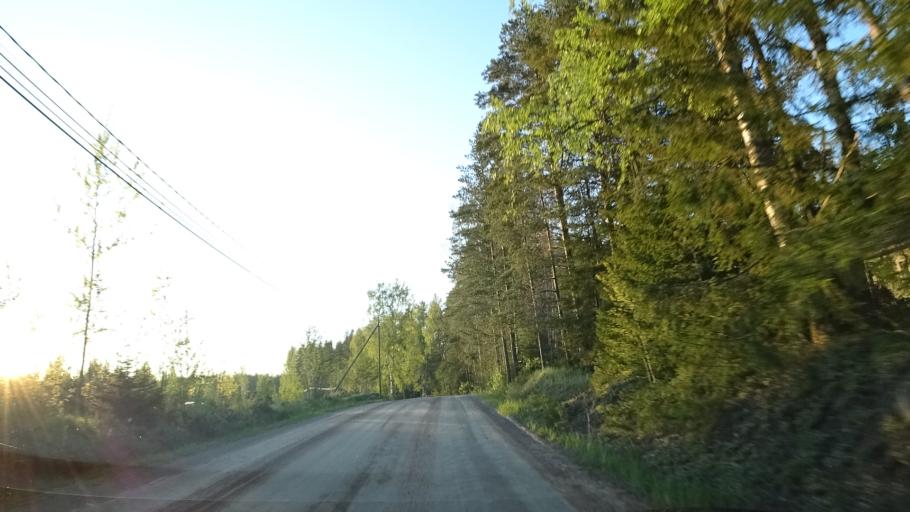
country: FI
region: Uusimaa
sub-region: Helsinki
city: Siuntio
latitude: 60.0702
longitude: 24.2055
